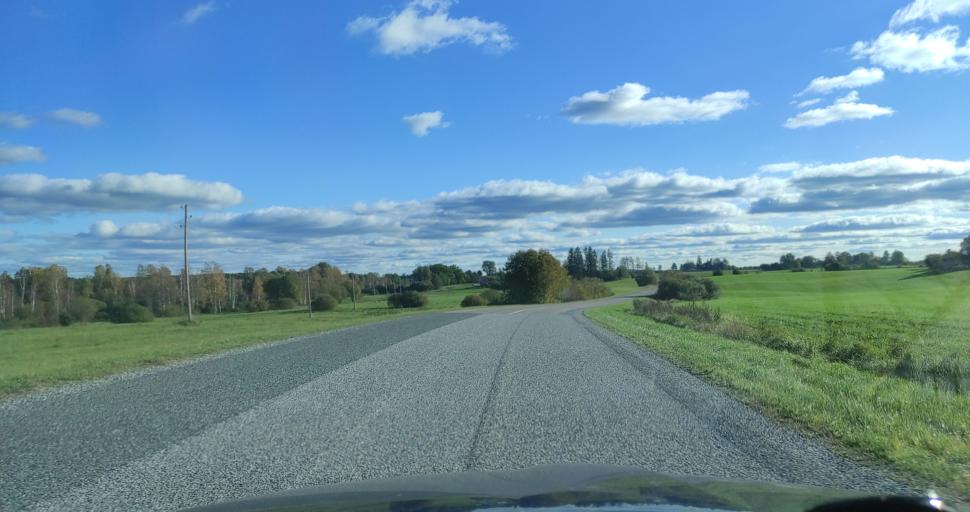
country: LV
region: Aizpute
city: Aizpute
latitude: 56.7635
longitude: 21.5405
